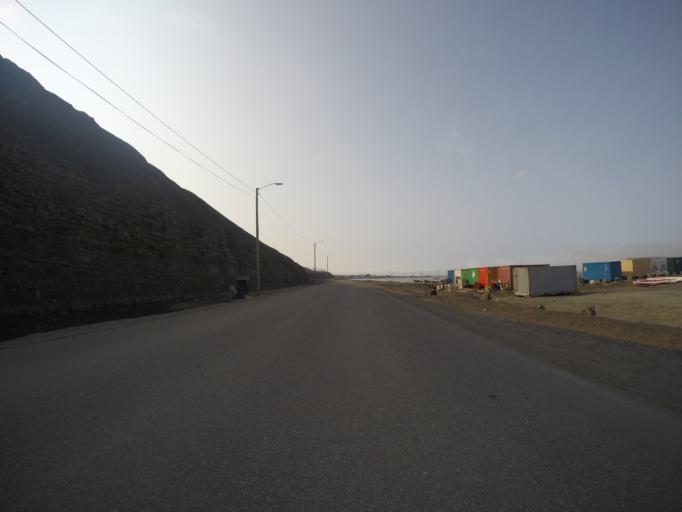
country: SJ
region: Svalbard
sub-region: Spitsbergen
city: Longyearbyen
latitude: 78.2274
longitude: 15.6042
